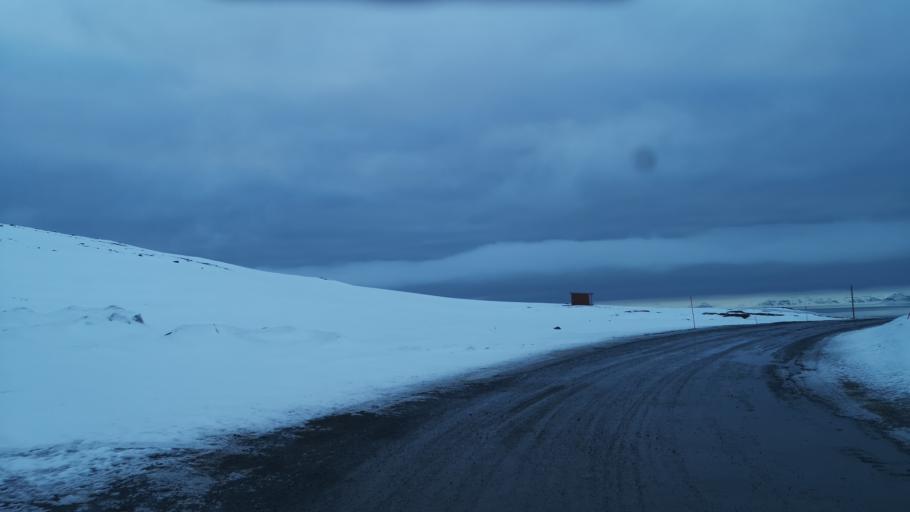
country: SJ
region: Svalbard
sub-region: Spitsbergen
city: Longyearbyen
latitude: 78.2349
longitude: 15.4586
